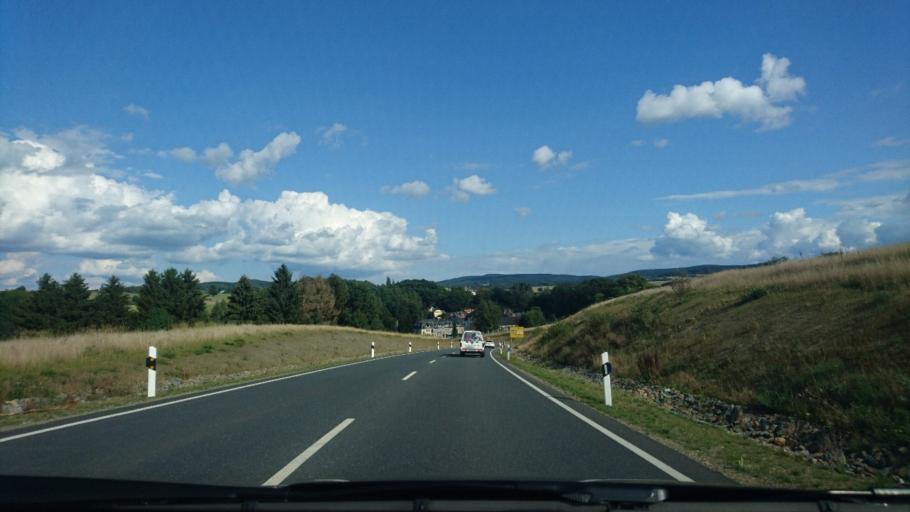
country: DE
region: Saxony
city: Rodewisch
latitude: 50.5357
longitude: 12.3963
